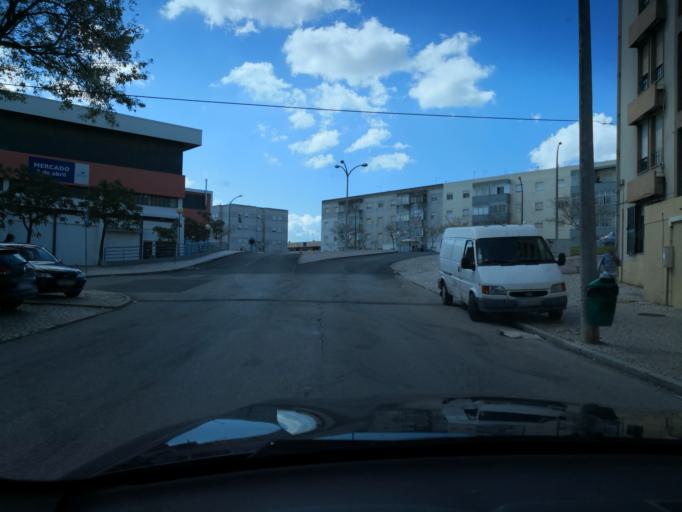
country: PT
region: Setubal
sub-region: Setubal
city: Setubal
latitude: 38.5245
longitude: -8.8688
